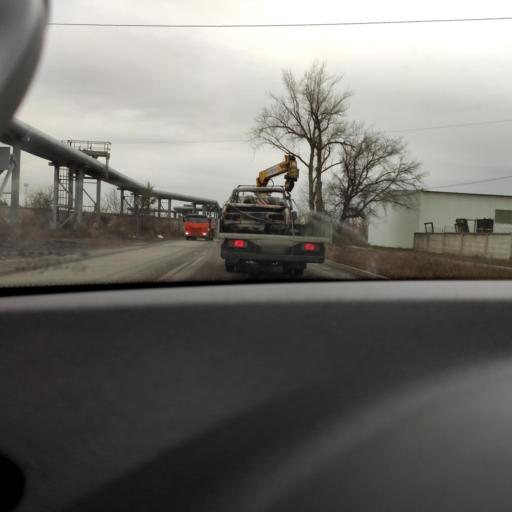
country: RU
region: Samara
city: Smyshlyayevka
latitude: 53.2063
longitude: 50.3028
